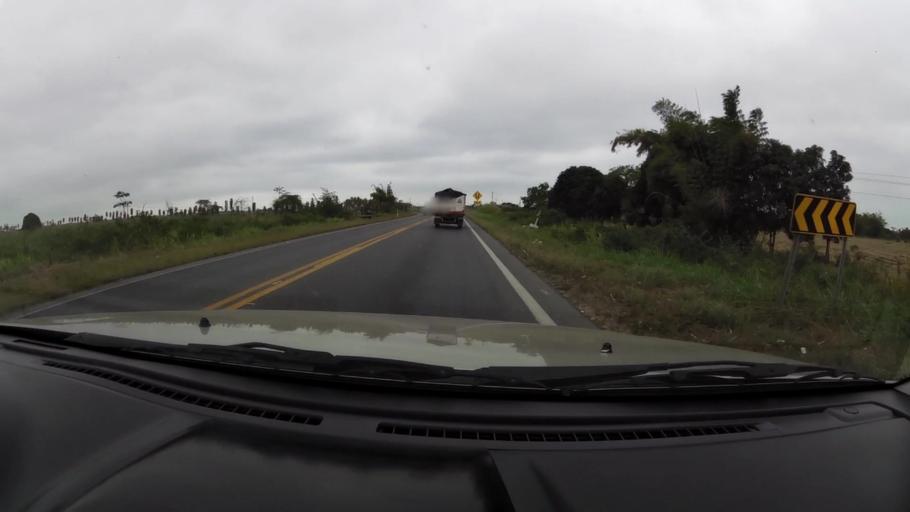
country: EC
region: Guayas
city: Naranjal
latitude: -2.5002
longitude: -79.5955
